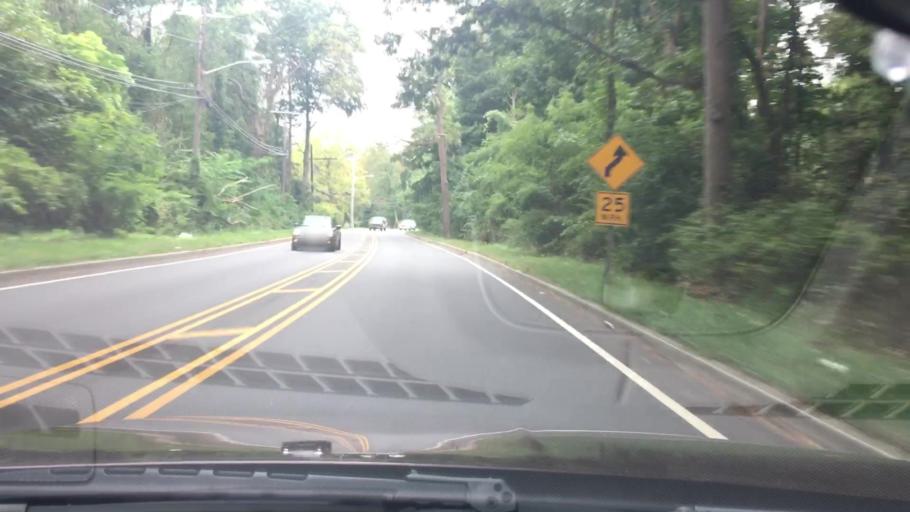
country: US
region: New York
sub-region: Nassau County
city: Farmingdale
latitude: 40.7380
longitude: -73.4594
